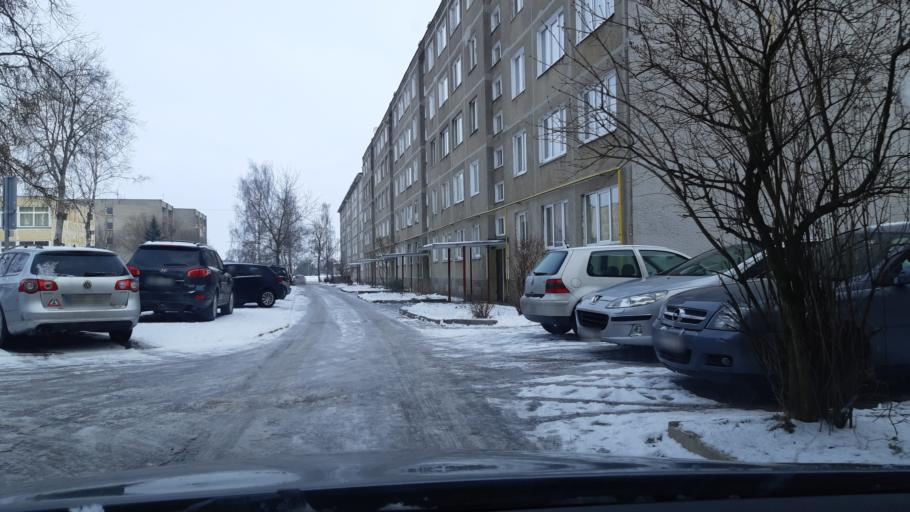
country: LT
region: Kauno apskritis
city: Kedainiai
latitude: 55.2920
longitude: 23.9848
